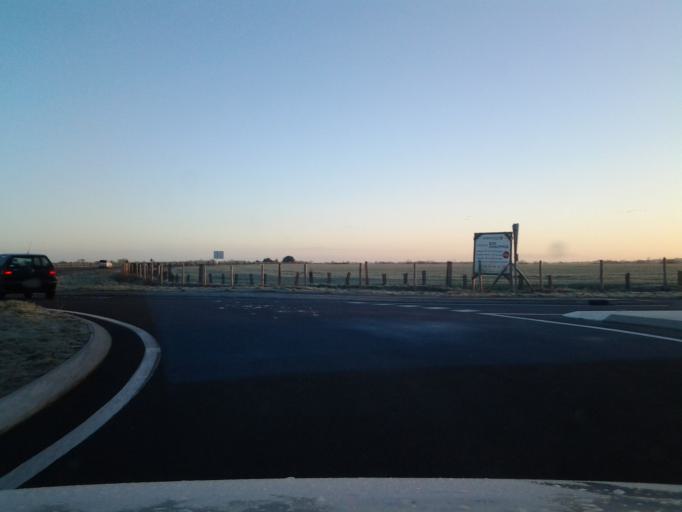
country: FR
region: Pays de la Loire
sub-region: Departement de la Vendee
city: La Gaubretiere
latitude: 46.9515
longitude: -1.0794
